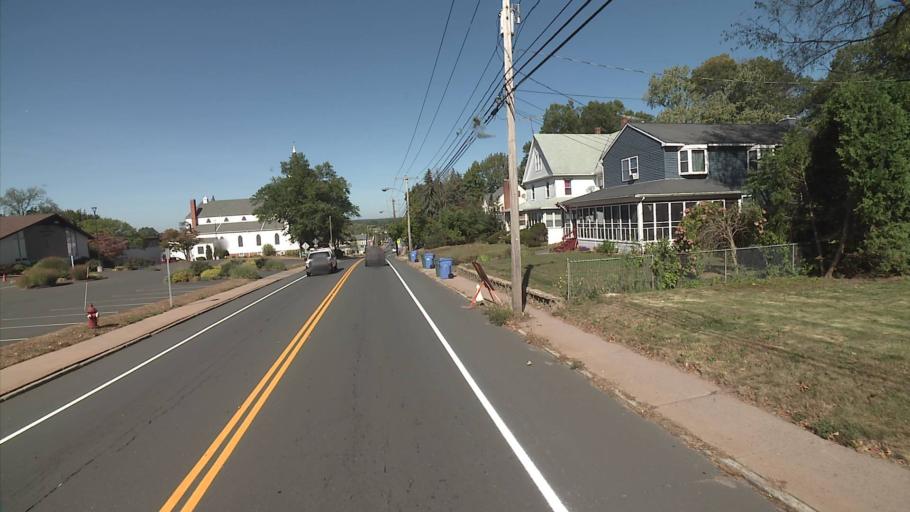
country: US
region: Connecticut
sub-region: Hartford County
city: Manchester
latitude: 41.7906
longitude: -72.5245
